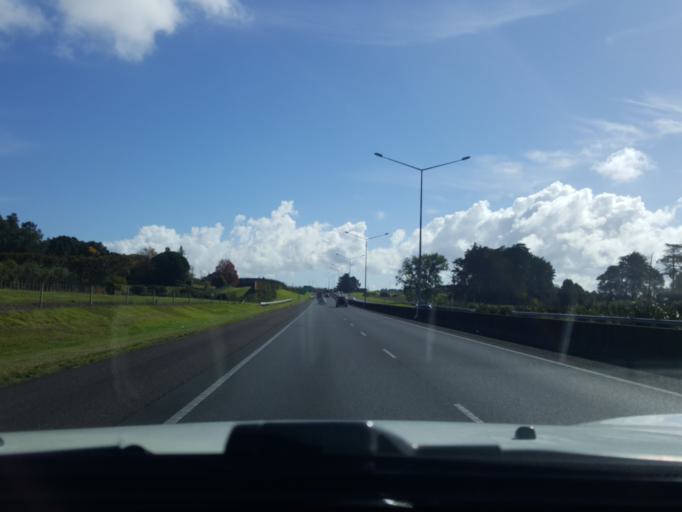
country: NZ
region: Auckland
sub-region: Auckland
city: Rosebank
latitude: -36.8011
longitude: 174.6014
